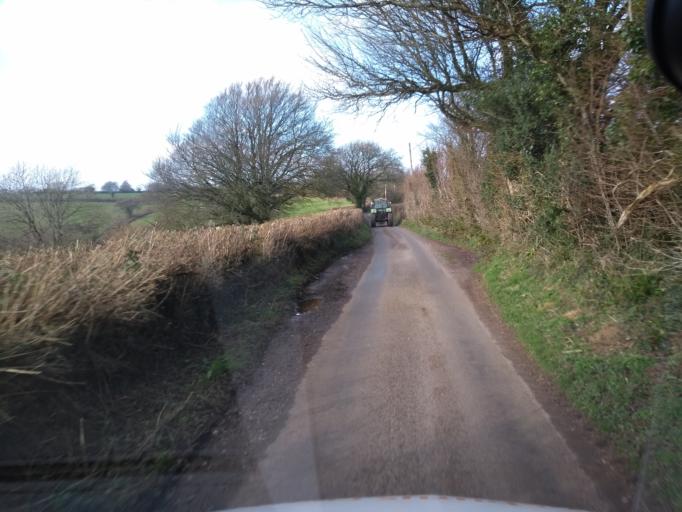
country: GB
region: England
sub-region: Somerset
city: Chard
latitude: 50.9339
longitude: -3.0243
